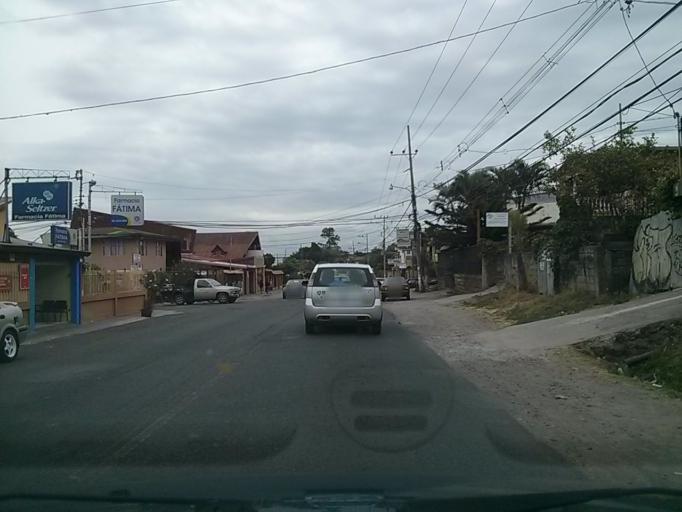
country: CR
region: San Jose
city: Patarra
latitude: 9.8895
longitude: -84.0398
